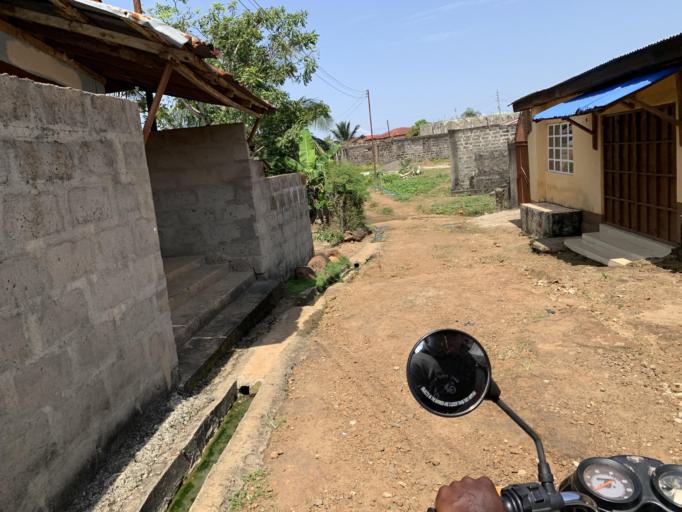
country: SL
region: Western Area
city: Hastings
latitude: 8.3761
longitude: -13.1314
